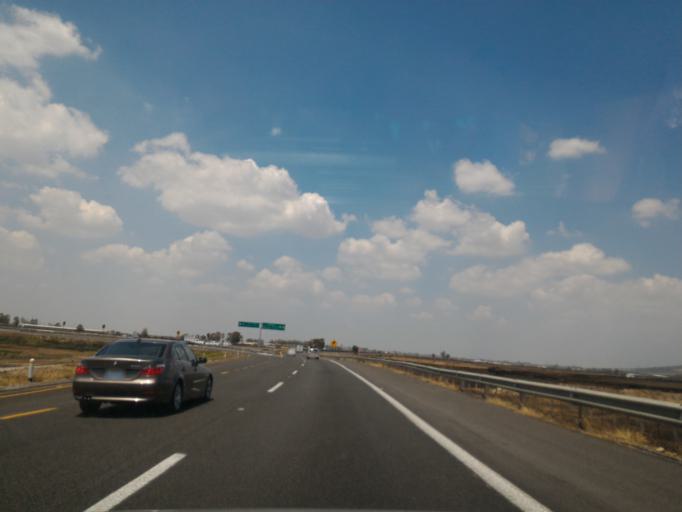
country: MX
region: Jalisco
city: Tepatitlan de Morelos
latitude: 20.9003
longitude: -102.6970
